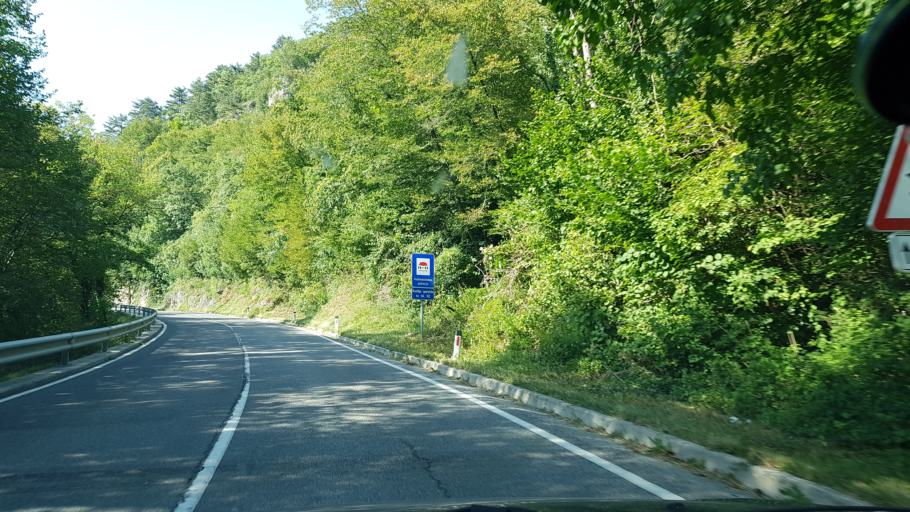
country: SI
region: Nova Gorica
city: Solkan
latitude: 45.9831
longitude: 13.6620
